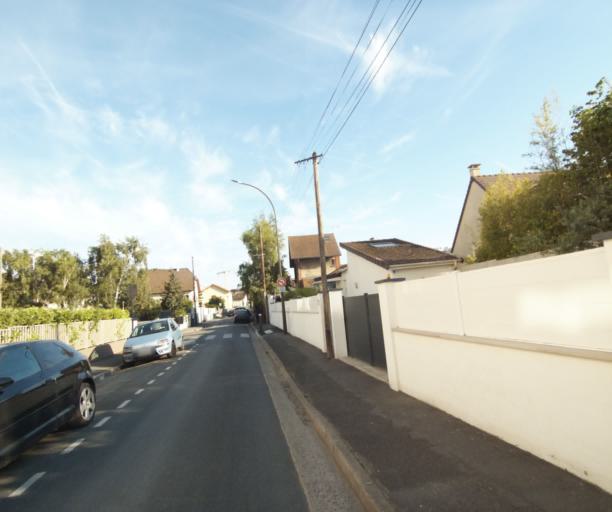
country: FR
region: Ile-de-France
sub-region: Departement du Val-d'Oise
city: Argenteuil
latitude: 48.9369
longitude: 2.2325
